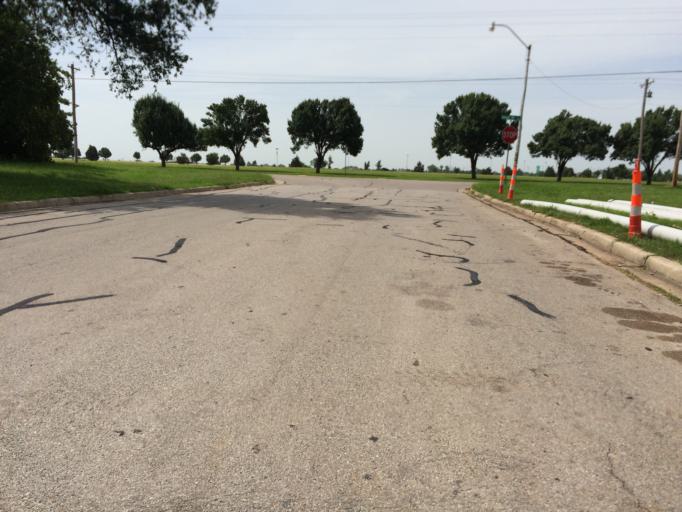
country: US
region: Oklahoma
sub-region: Cleveland County
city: Norman
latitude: 35.1901
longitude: -97.4104
